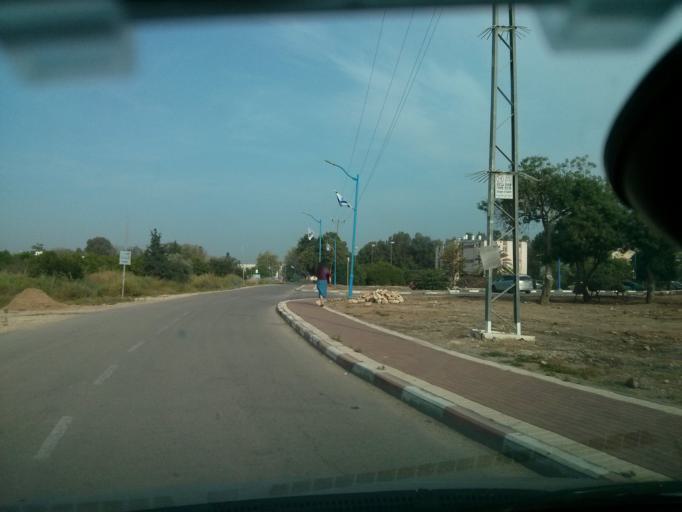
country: IL
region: Central District
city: Gan Yavne
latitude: 31.6981
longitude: 34.7127
